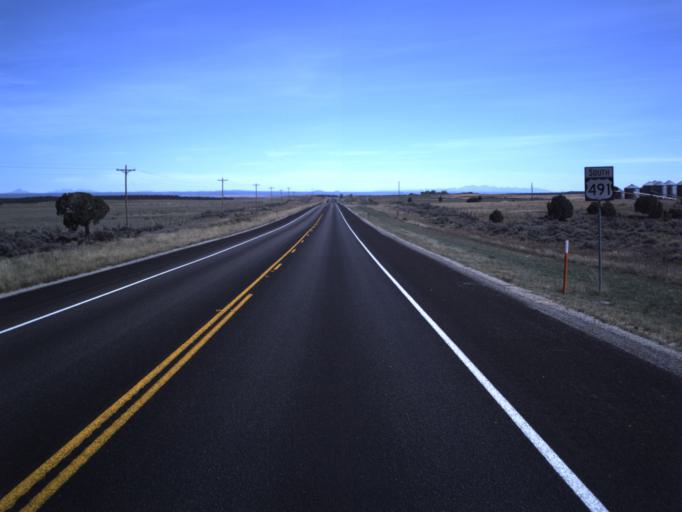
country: US
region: Utah
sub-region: San Juan County
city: Monticello
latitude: 37.8557
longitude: -109.1889
